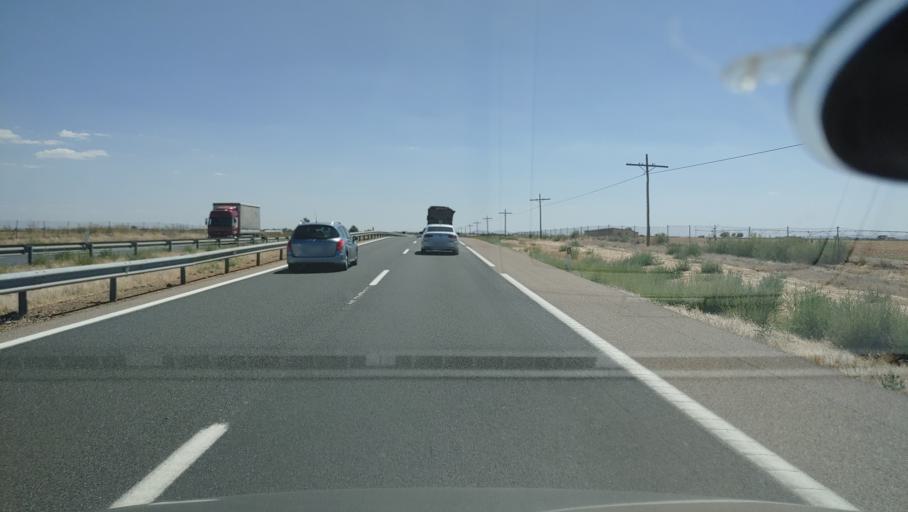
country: ES
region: Castille-La Mancha
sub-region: Provincia de Ciudad Real
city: Villarta de San Juan
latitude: 39.1509
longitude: -3.3871
